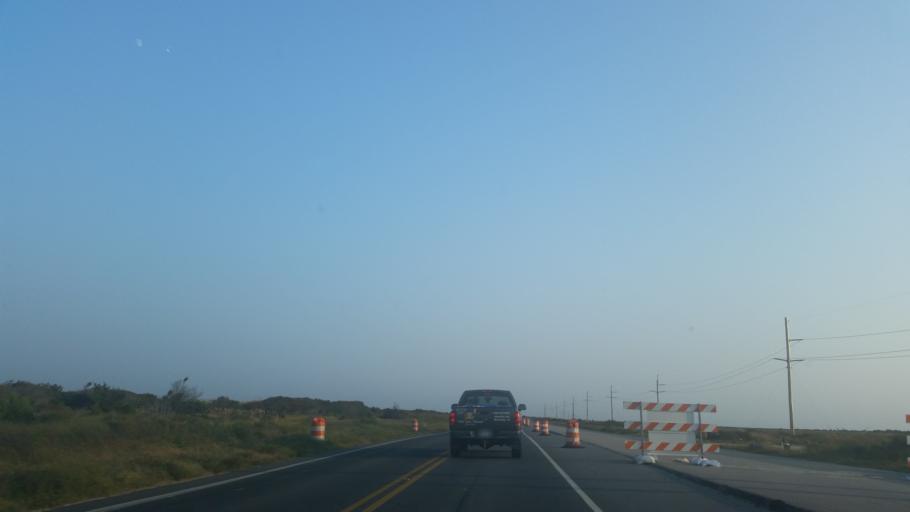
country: US
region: North Carolina
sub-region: Dare County
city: Wanchese
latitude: 35.6759
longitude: -75.4807
